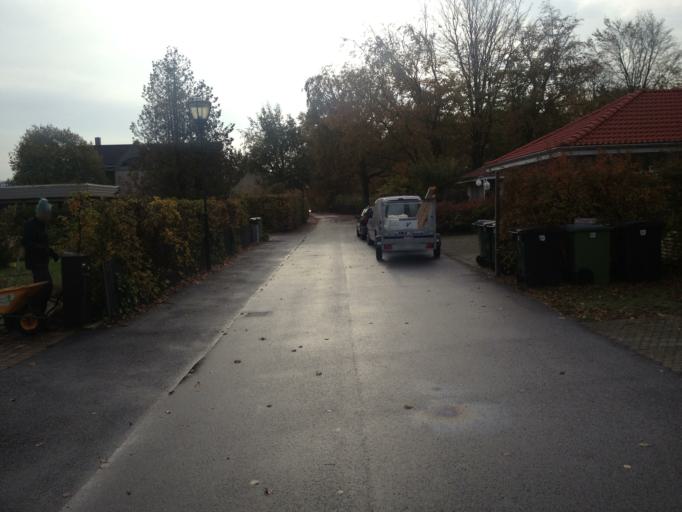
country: SE
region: Skane
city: Bjarred
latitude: 55.7216
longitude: 13.0111
